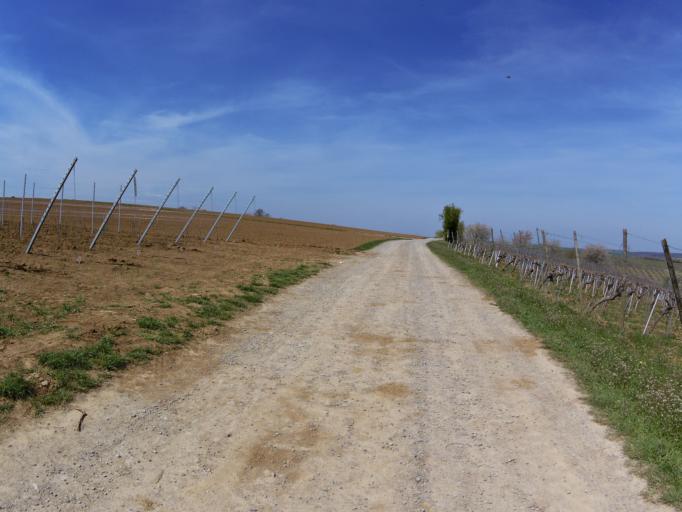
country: DE
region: Bavaria
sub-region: Regierungsbezirk Unterfranken
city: Mainstockheim
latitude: 49.7981
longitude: 10.1462
